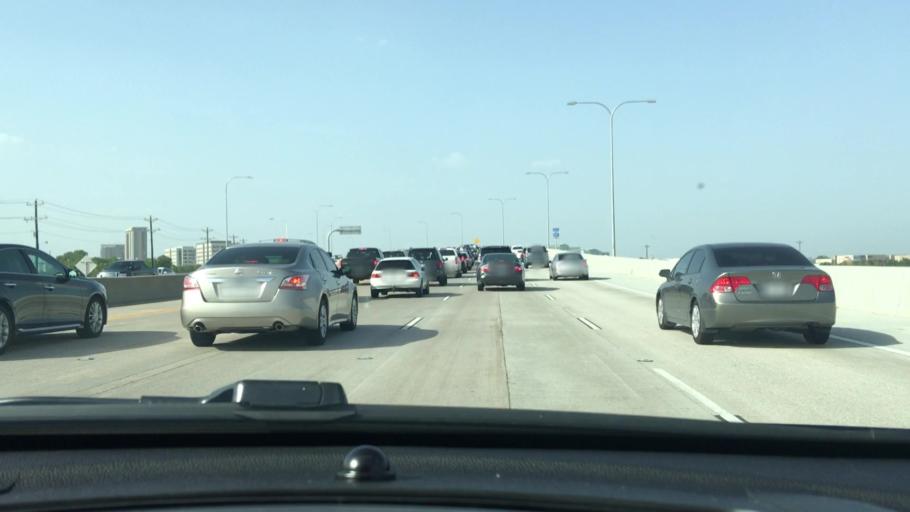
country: US
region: Texas
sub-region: Denton County
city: The Colony
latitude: 33.0603
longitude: -96.8261
